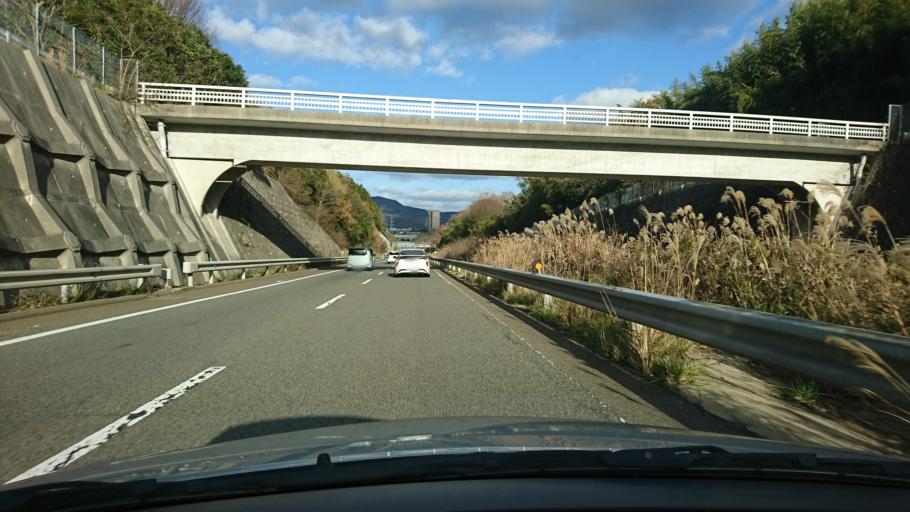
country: JP
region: Hyogo
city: Kobe
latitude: 34.7465
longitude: 135.1321
